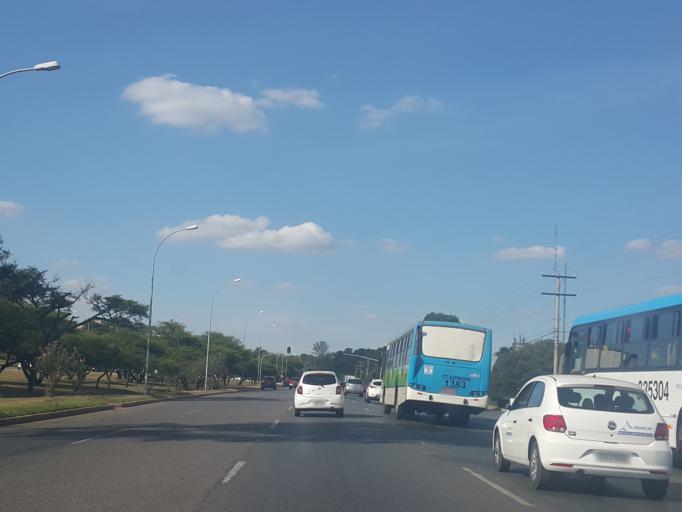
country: BR
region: Federal District
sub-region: Brasilia
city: Brasilia
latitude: -15.8088
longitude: -47.9337
